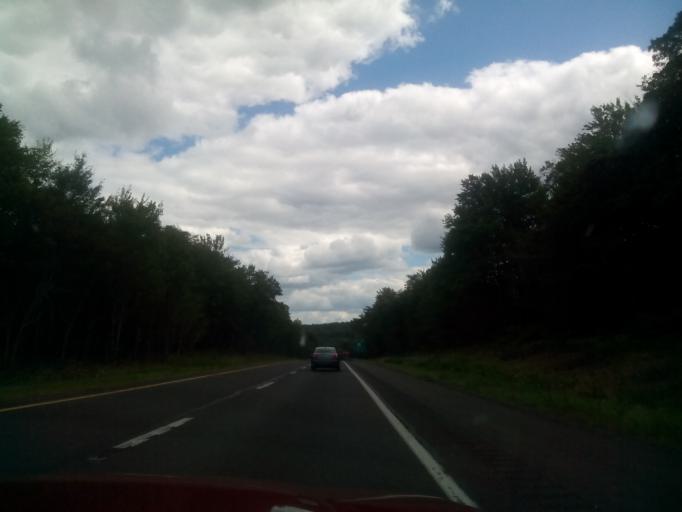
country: US
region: Pennsylvania
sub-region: Carbon County
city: Towamensing Trails
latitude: 41.0815
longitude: -75.6195
